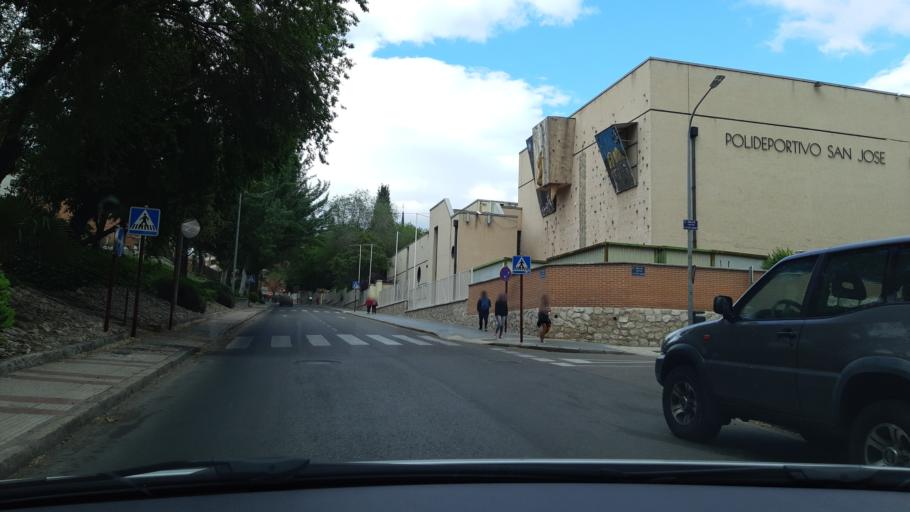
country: ES
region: Castille-La Mancha
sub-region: Provincia de Guadalajara
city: Guadalajara
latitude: 40.6309
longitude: -3.1691
